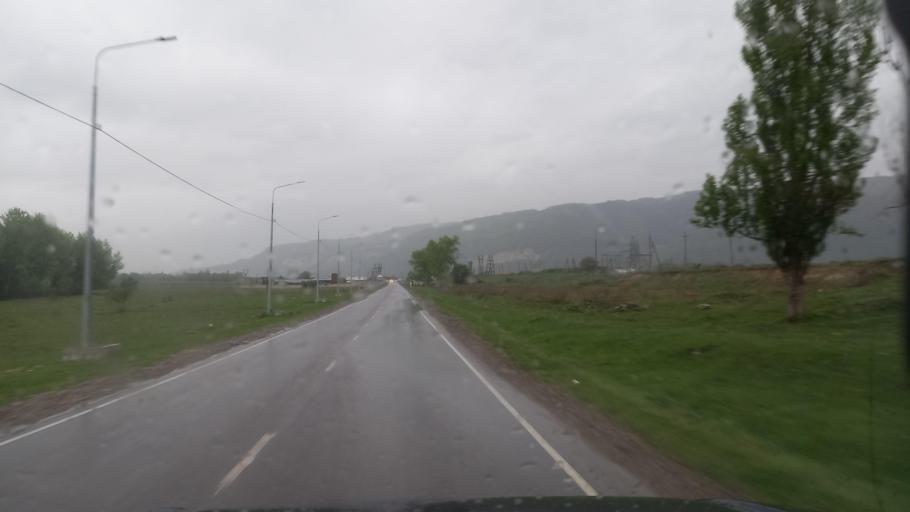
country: RU
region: Kabardino-Balkariya
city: Zhankhoteko
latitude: 43.5882
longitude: 43.2203
